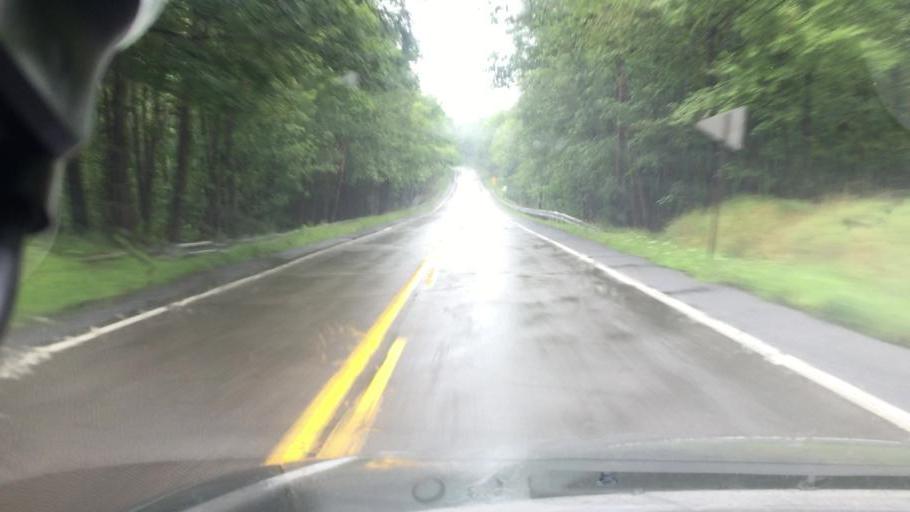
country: US
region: Pennsylvania
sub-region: Luzerne County
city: White Haven
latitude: 41.0409
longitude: -75.8251
